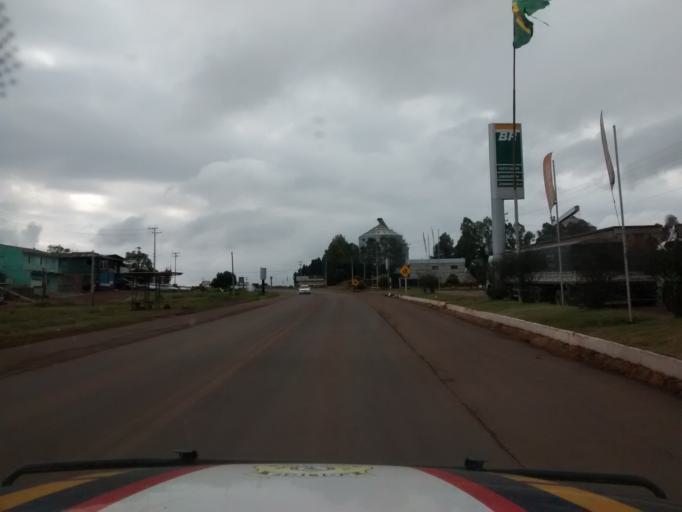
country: BR
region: Rio Grande do Sul
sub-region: Lagoa Vermelha
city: Lagoa Vermelha
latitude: -28.2136
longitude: -51.5103
